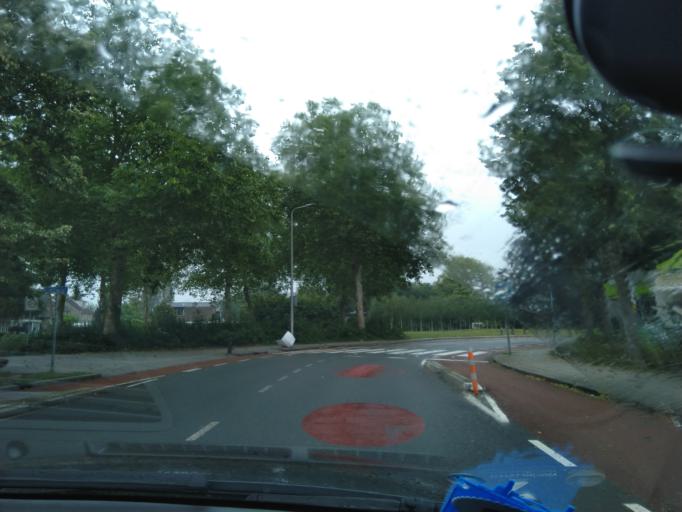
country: NL
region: Overijssel
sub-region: Gemeente Twenterand
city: Den Ham
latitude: 52.3619
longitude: 6.4668
